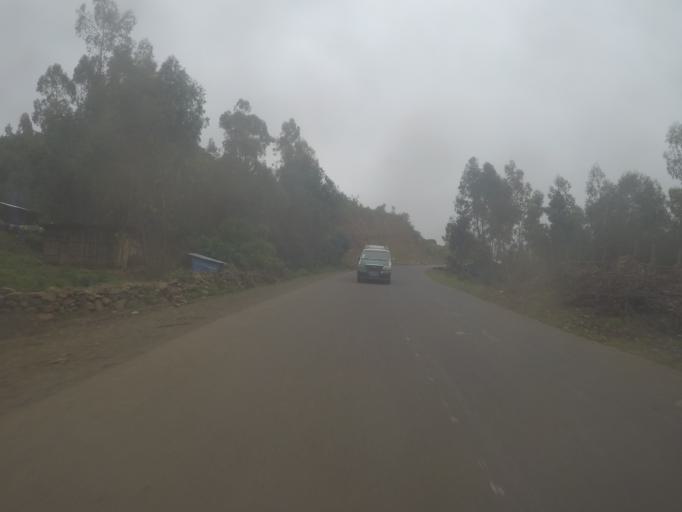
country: ET
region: Amhara
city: Gondar
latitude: 12.7414
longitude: 37.5143
